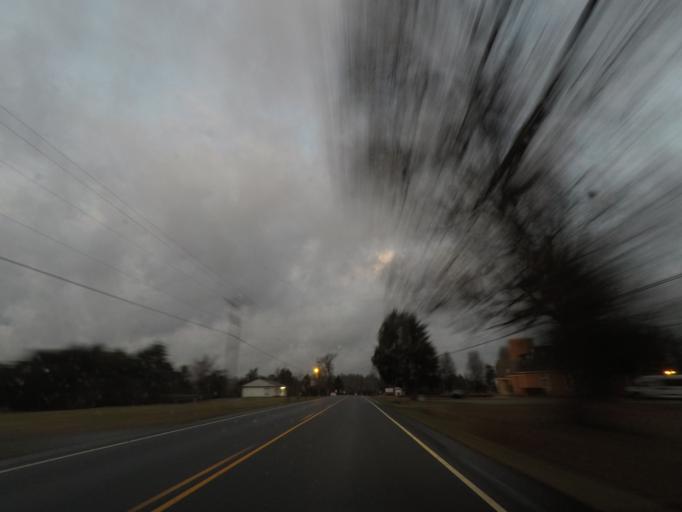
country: US
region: North Carolina
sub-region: Orange County
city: Hillsborough
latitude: 36.1574
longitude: -79.1285
